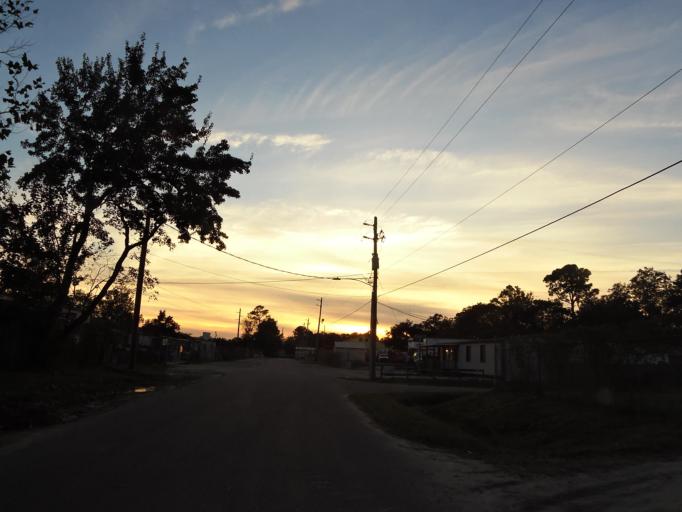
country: US
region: Florida
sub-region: Duval County
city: Jacksonville
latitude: 30.3562
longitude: -81.7326
